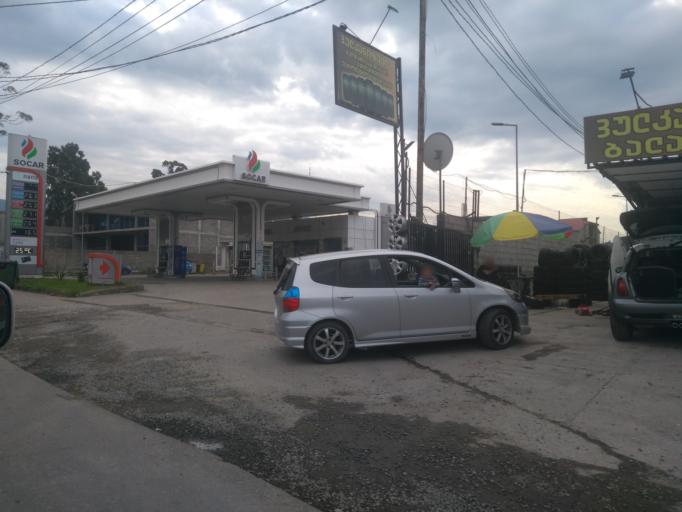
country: GE
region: Ajaria
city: Batumi
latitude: 41.6063
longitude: 41.6286
